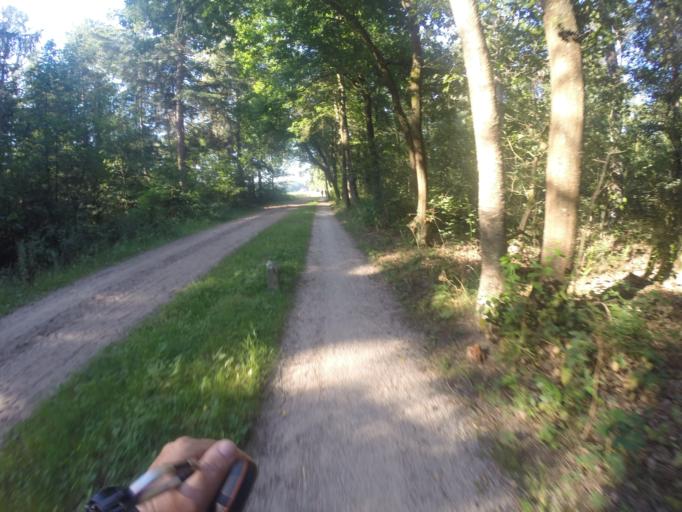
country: NL
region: Gelderland
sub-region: Gemeente Lochem
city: Almen
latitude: 52.1167
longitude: 6.3521
